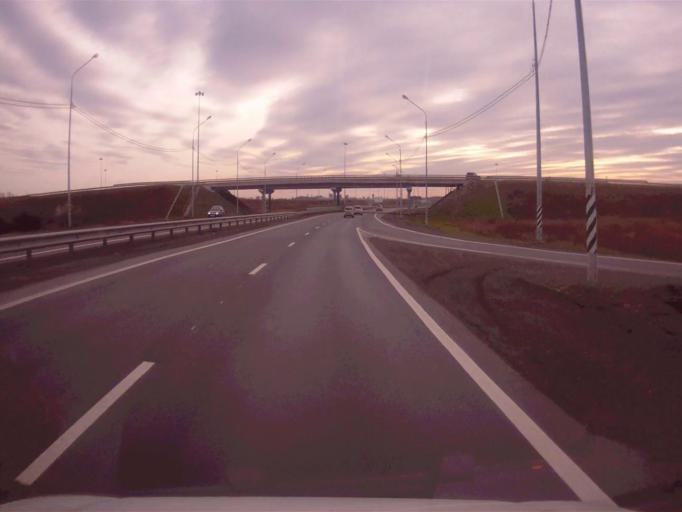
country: RU
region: Chelyabinsk
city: Novosineglazovskiy
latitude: 55.0033
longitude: 61.4540
